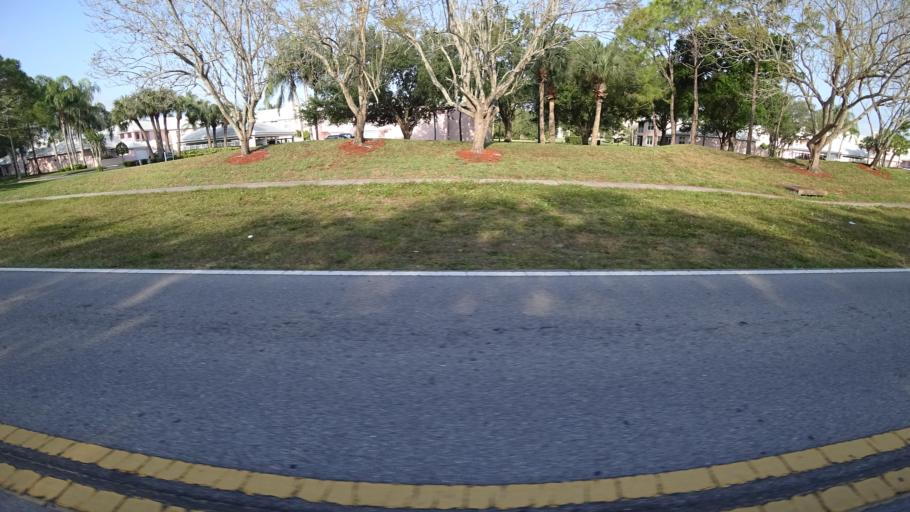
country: US
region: Florida
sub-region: Manatee County
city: South Bradenton
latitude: 27.4649
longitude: -82.6041
